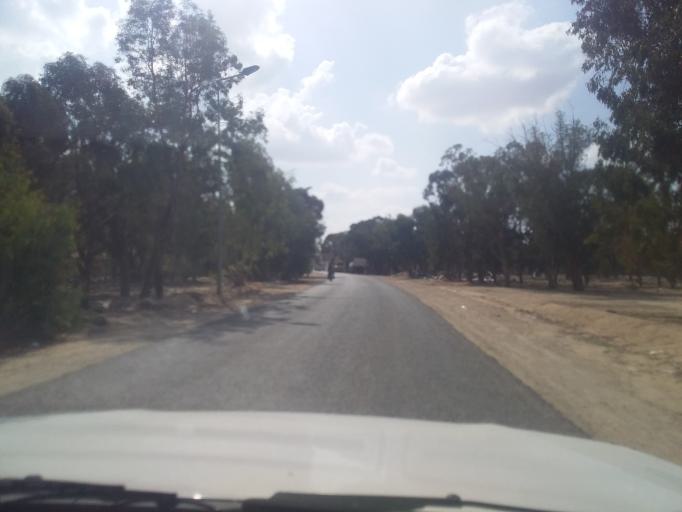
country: TN
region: Qabis
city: Gabes
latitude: 33.6234
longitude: 10.2779
